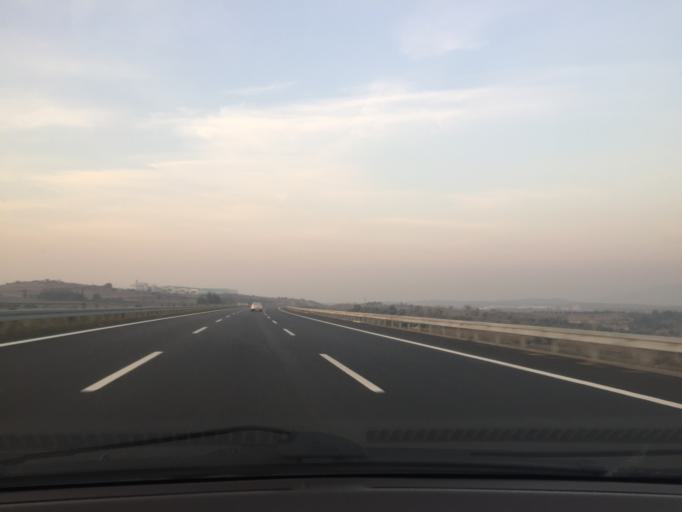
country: TR
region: Bursa
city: Karacabey
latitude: 40.2604
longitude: 28.4824
